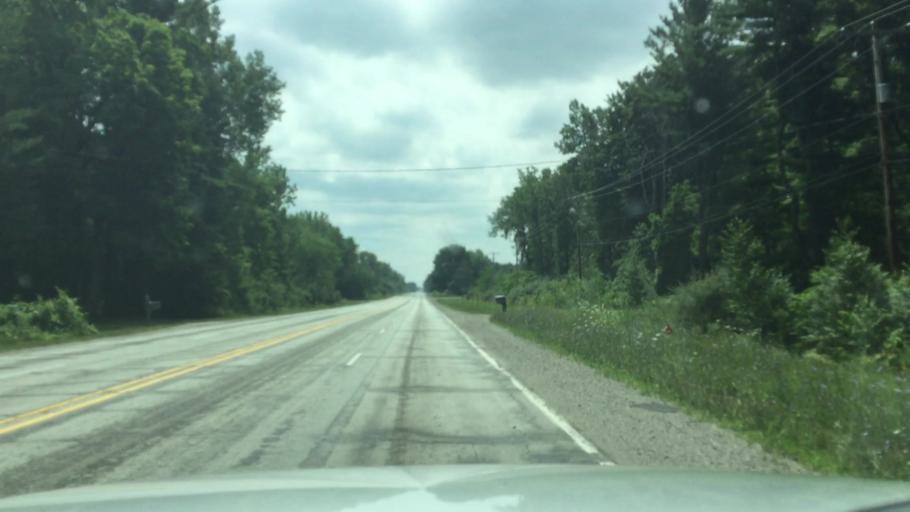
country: US
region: Michigan
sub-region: Saginaw County
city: Birch Run
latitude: 43.2857
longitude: -83.7962
